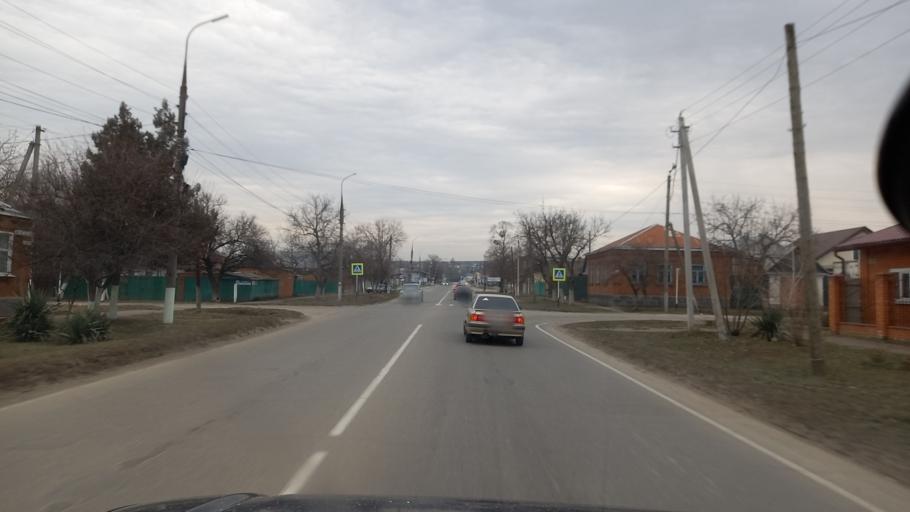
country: RU
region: Adygeya
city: Maykop
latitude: 44.5984
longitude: 40.1302
